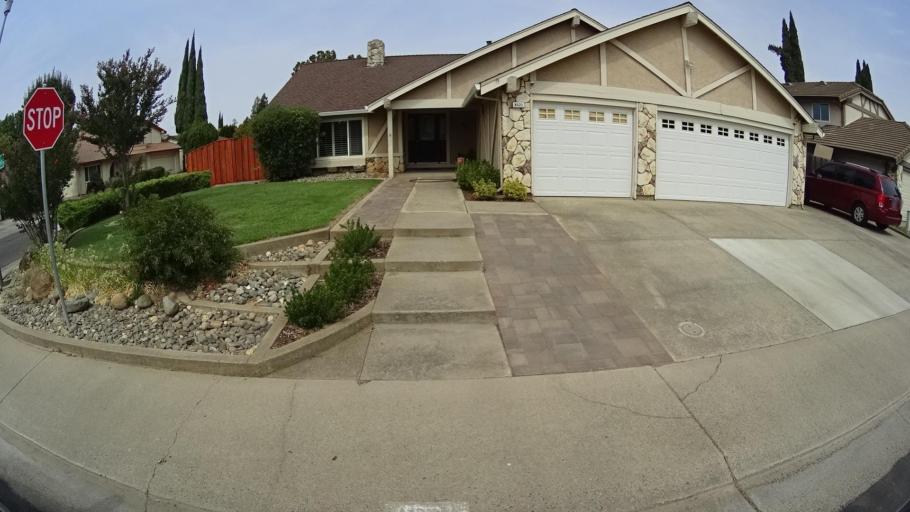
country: US
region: California
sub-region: Sacramento County
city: Elk Grove
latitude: 38.4186
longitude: -121.3885
